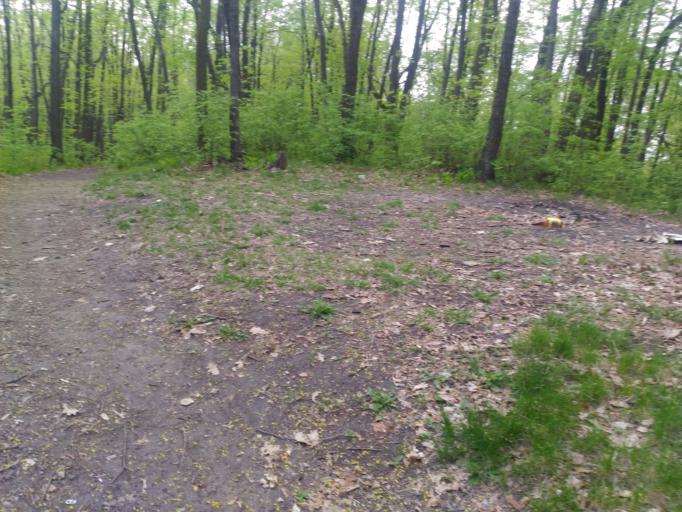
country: RU
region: Ulyanovsk
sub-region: Ulyanovskiy Rayon
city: Ulyanovsk
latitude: 54.2718
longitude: 48.3417
